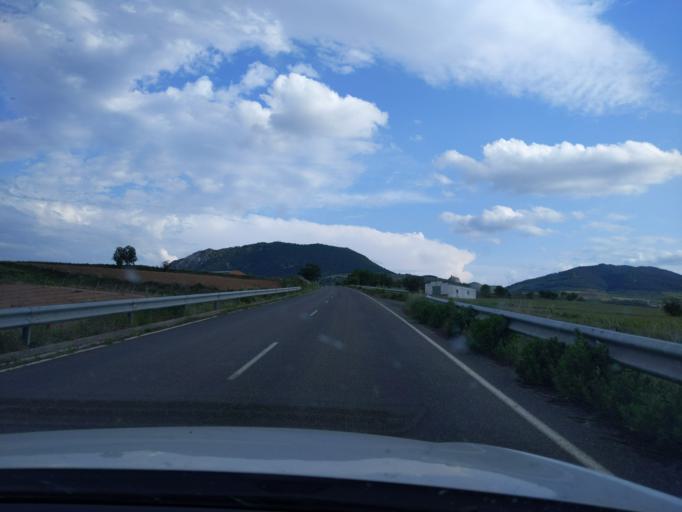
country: ES
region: La Rioja
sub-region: Provincia de La Rioja
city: Clavijo
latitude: 42.3765
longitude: -2.4235
